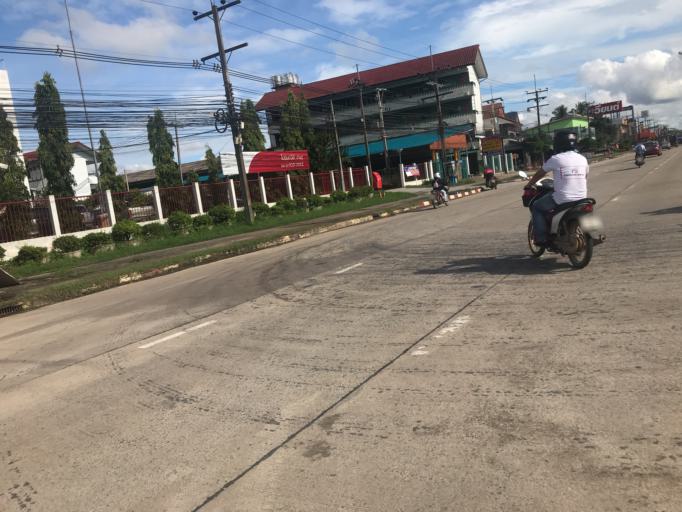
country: TH
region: Chiang Rai
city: Chiang Rai
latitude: 19.9773
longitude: 99.8594
